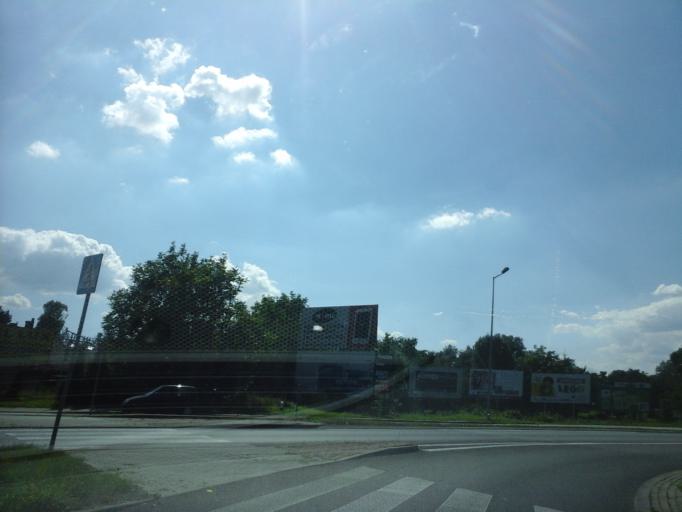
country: PL
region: Lesser Poland Voivodeship
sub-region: Powiat oswiecimski
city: Oswiecim
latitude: 50.0314
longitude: 19.2193
